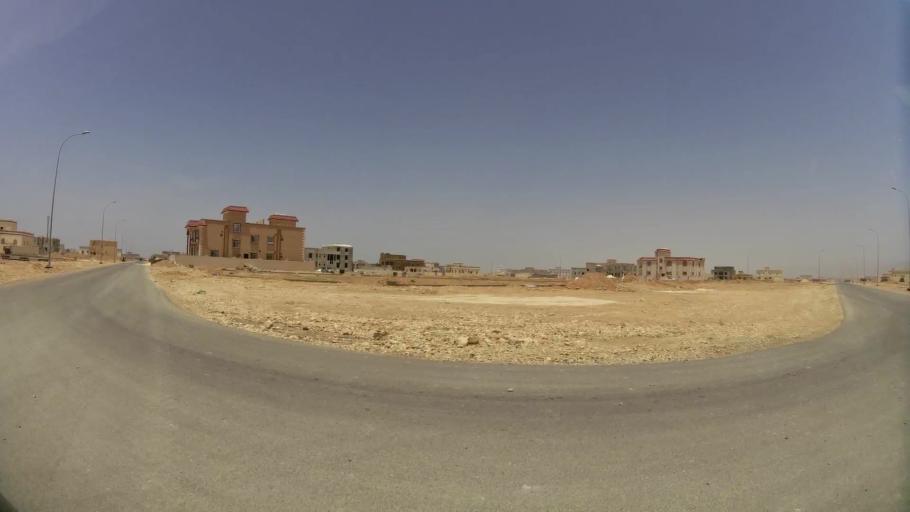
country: OM
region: Zufar
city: Salalah
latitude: 17.0977
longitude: 54.1837
